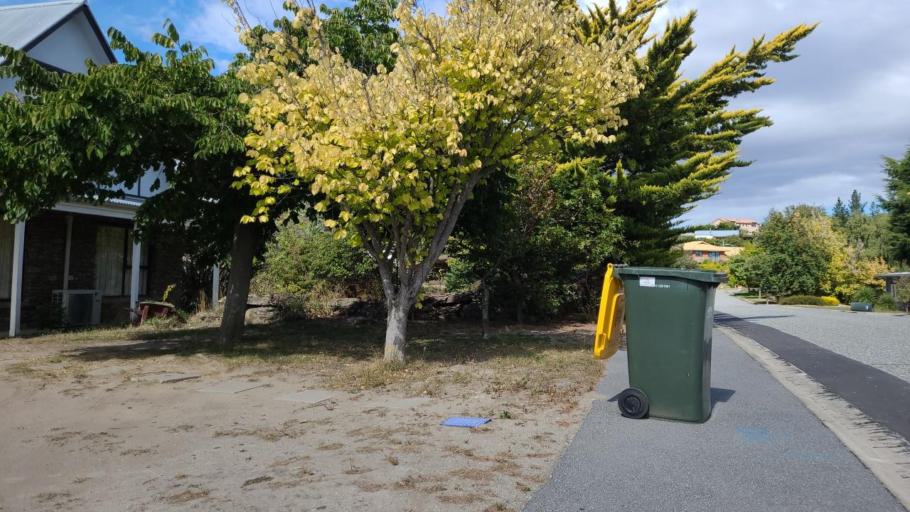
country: NZ
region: Otago
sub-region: Queenstown-Lakes District
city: Wanaka
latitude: -45.2610
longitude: 169.3776
